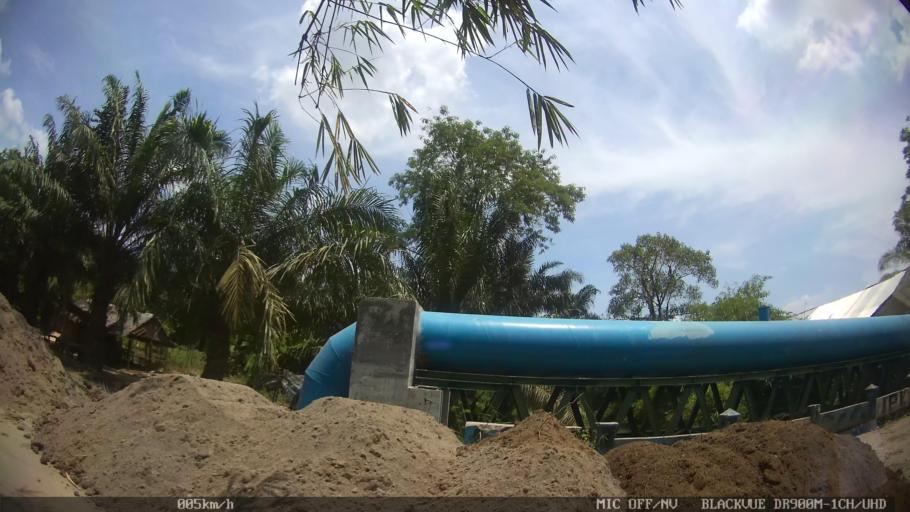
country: ID
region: North Sumatra
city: Binjai
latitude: 3.5932
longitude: 98.5355
